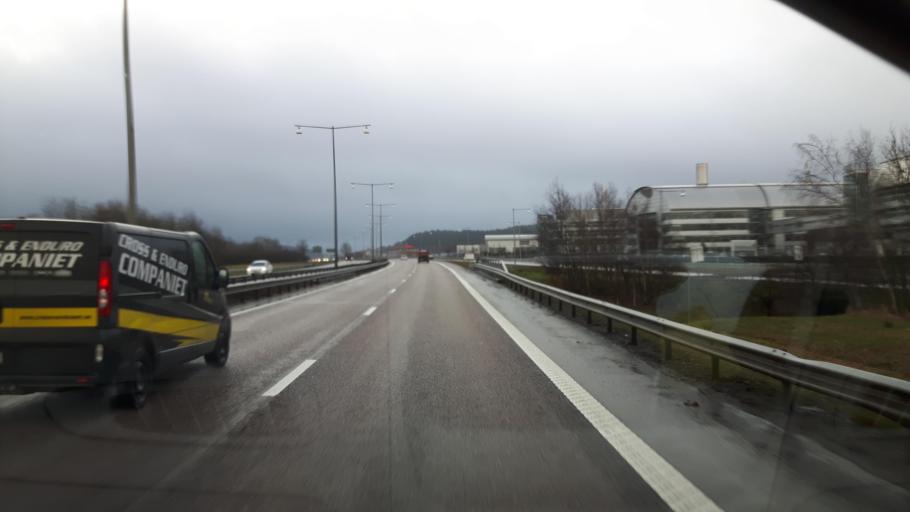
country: SE
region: Vaestra Goetaland
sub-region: Molndal
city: Moelndal
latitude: 57.6468
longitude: 12.0227
